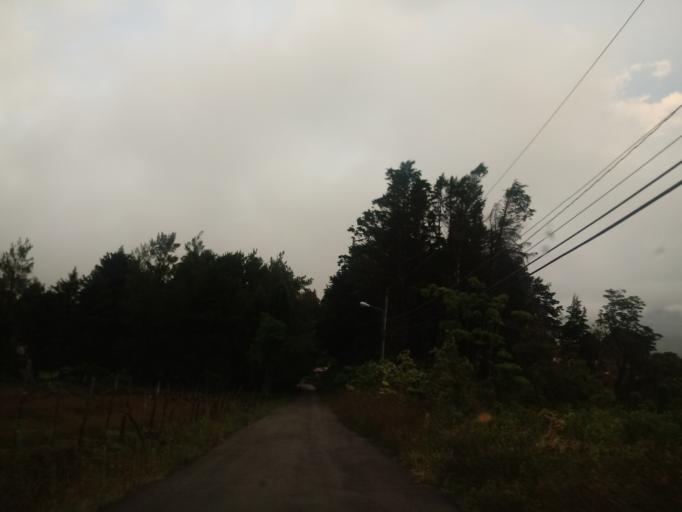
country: CR
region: Heredia
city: Angeles
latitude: 10.0359
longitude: -84.0389
